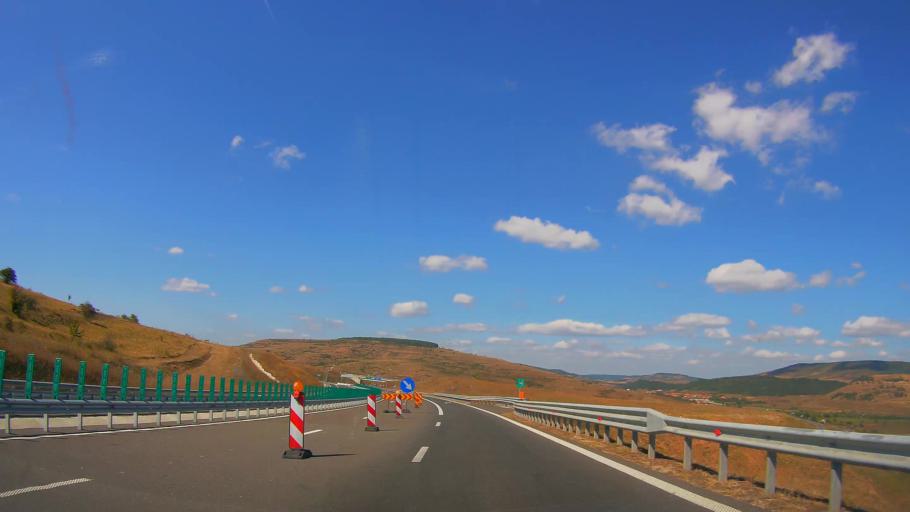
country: RO
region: Cluj
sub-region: Comuna Baciu
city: Mera
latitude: 46.8058
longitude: 23.4256
